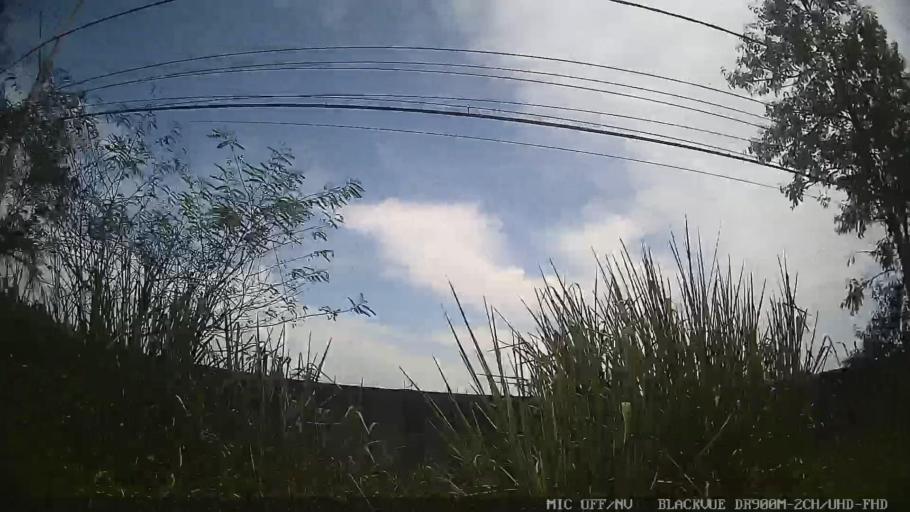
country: BR
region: Sao Paulo
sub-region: Santa Isabel
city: Santa Isabel
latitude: -23.3856
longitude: -46.1736
